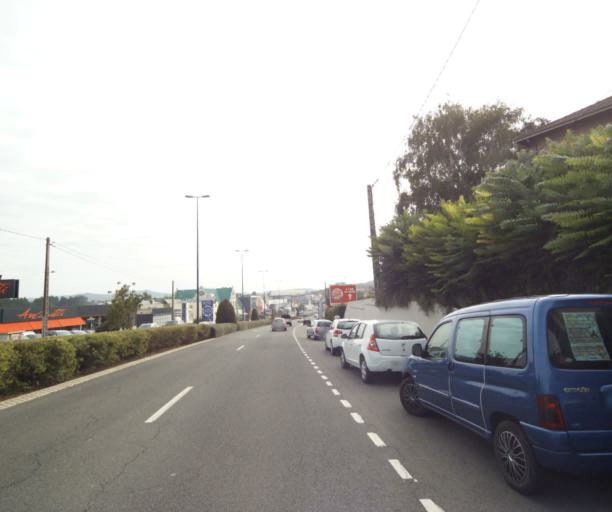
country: FR
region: Auvergne
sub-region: Departement du Puy-de-Dome
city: Aubiere
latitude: 45.7684
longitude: 3.1243
